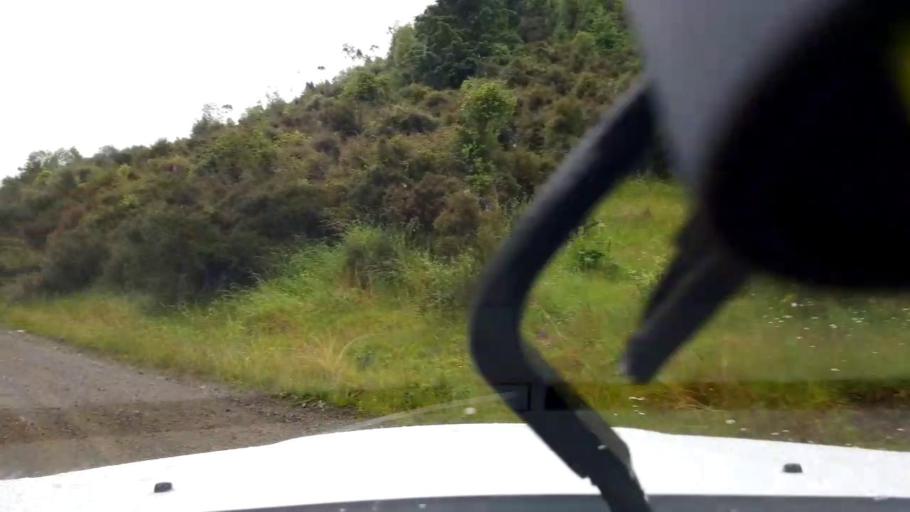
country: NZ
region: Canterbury
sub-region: Timaru District
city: Pleasant Point
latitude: -44.0442
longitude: 171.0193
